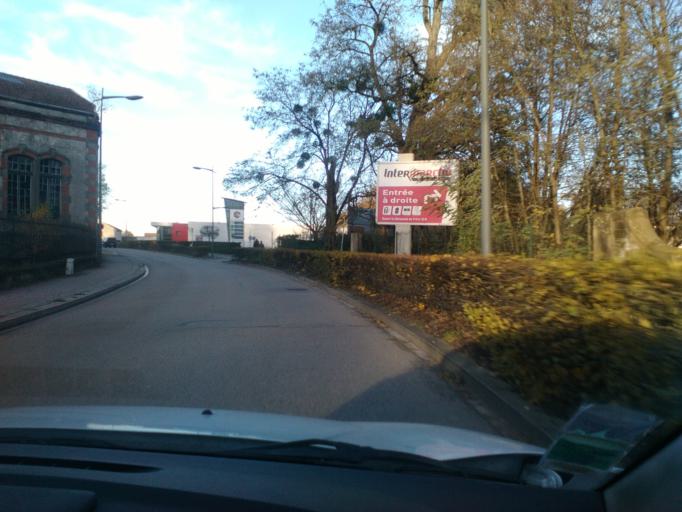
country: FR
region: Lorraine
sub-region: Departement des Vosges
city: Epinal
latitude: 48.1878
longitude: 6.4429
